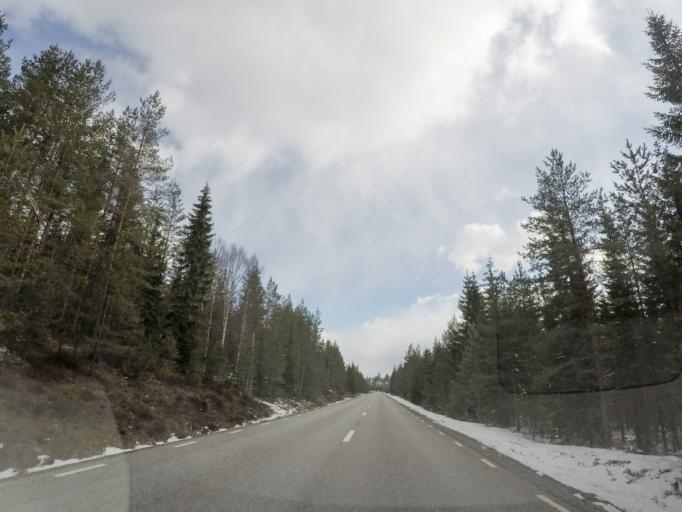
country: SE
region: OErebro
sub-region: Ljusnarsbergs Kommun
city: Kopparberg
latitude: 59.8812
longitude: 15.1214
